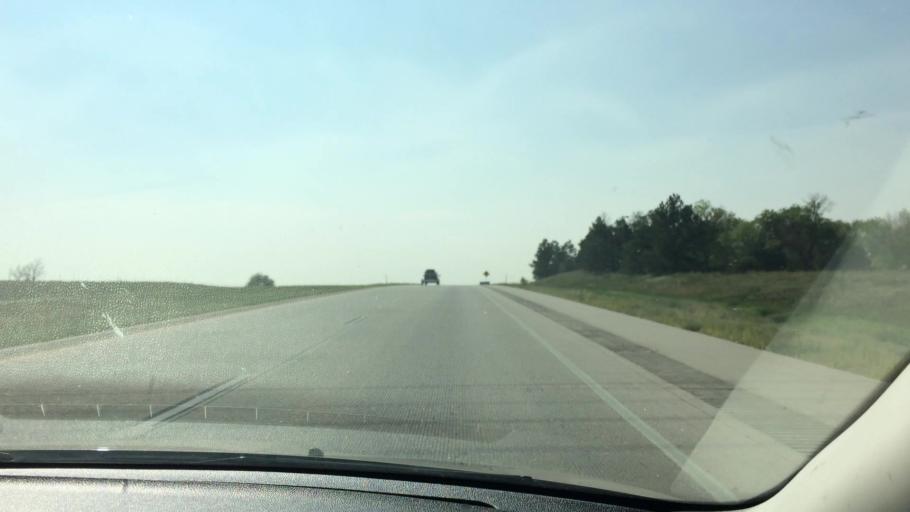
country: US
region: Colorado
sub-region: Adams County
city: Bennett
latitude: 39.7359
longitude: -104.3958
